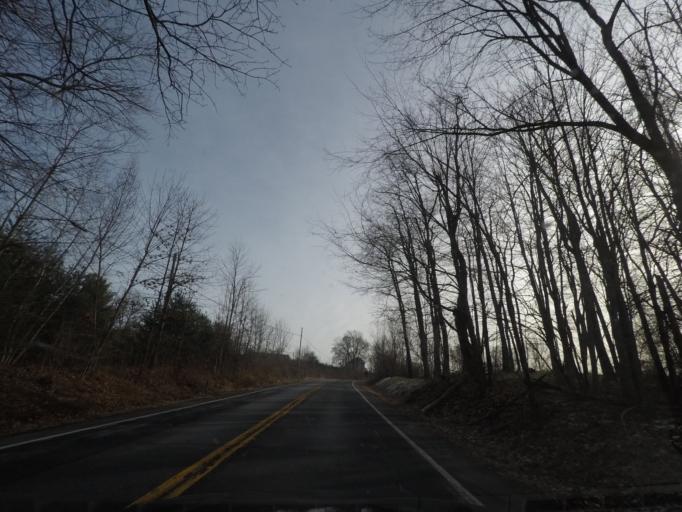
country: US
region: New York
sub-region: Saratoga County
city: Stillwater
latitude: 42.9897
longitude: -73.6998
